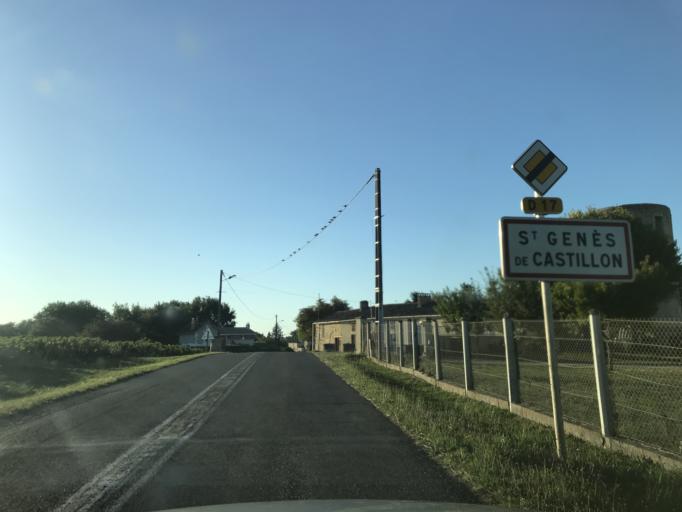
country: FR
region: Aquitaine
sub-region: Departement de la Gironde
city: Lussac
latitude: 44.8957
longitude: -0.0594
